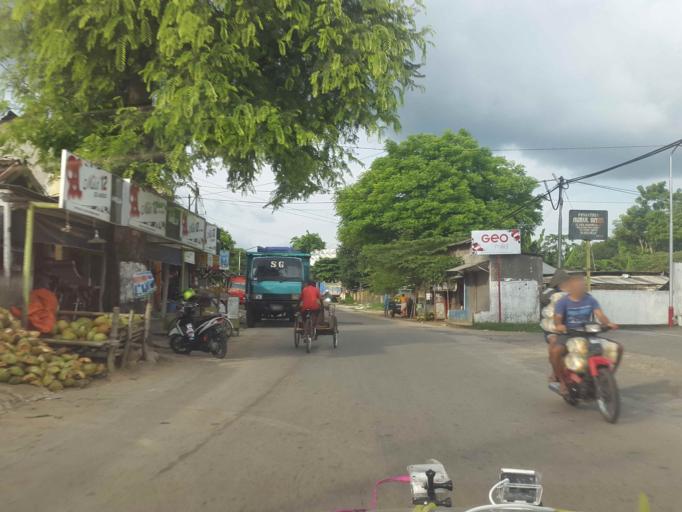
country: ID
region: East Java
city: Senmasen
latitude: -6.9985
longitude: 113.8660
